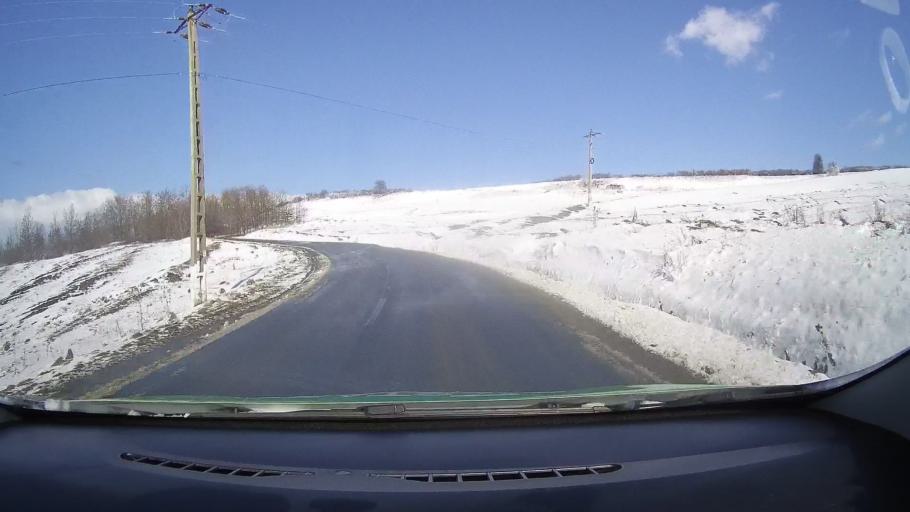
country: RO
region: Sibiu
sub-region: Comuna Rosia
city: Rosia
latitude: 45.8066
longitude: 24.2916
